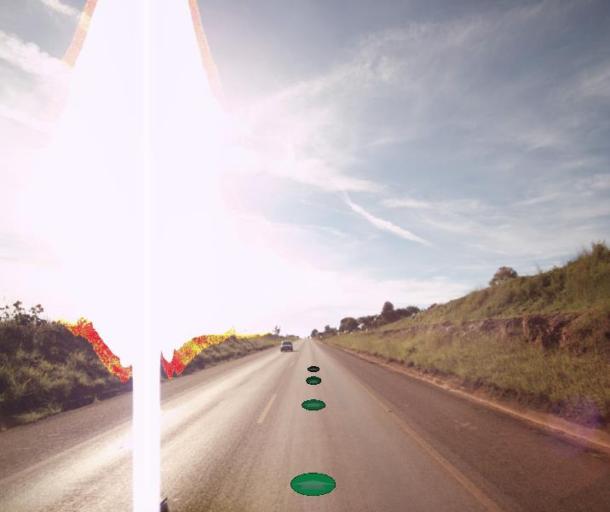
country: BR
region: Federal District
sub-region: Brasilia
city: Brasilia
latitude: -15.7375
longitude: -48.3954
